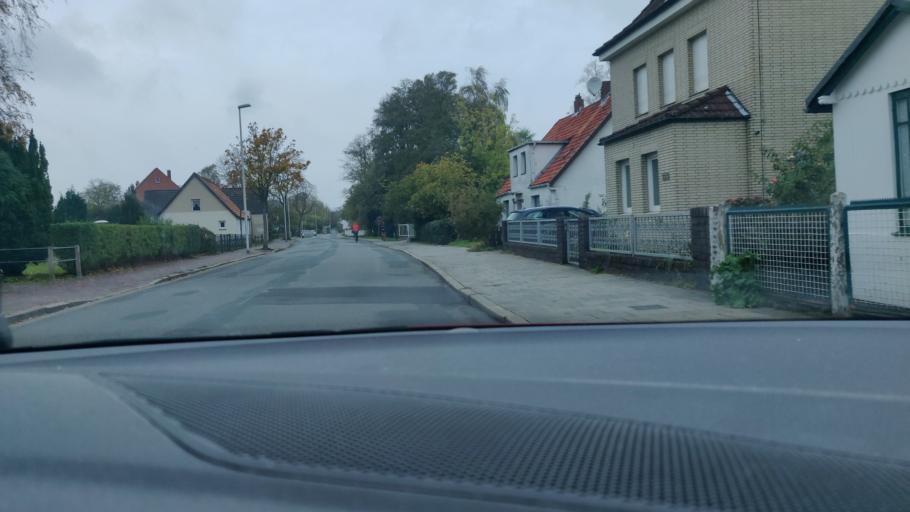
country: DE
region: Lower Saxony
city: Cuxhaven
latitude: 53.8798
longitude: 8.6814
